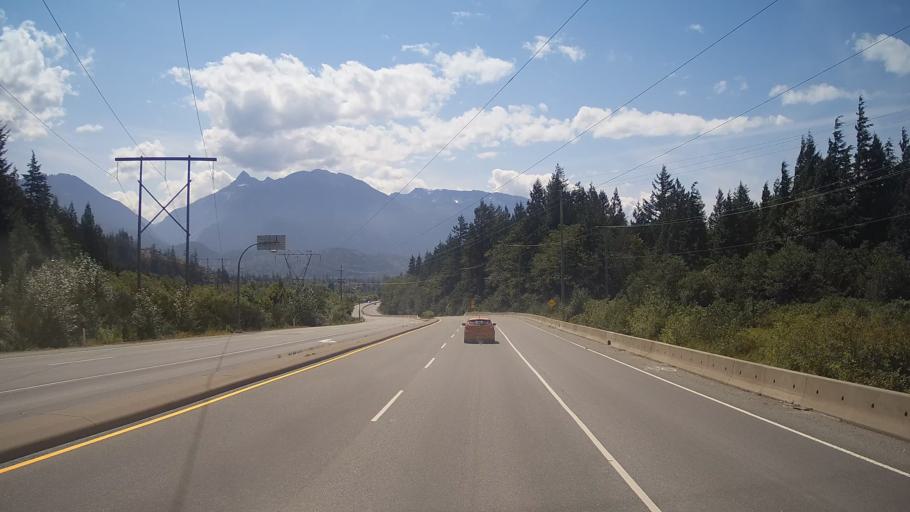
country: CA
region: British Columbia
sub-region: Greater Vancouver Regional District
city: Lions Bay
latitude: 49.7655
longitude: -123.1380
